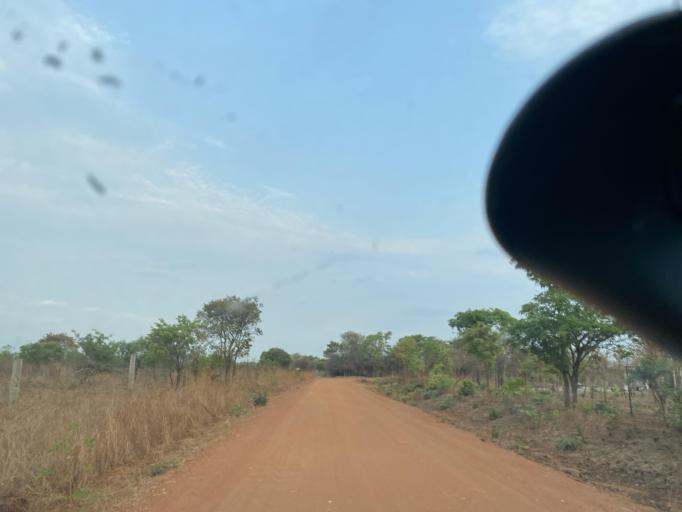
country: ZM
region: Lusaka
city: Chongwe
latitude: -15.2233
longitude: 28.5903
